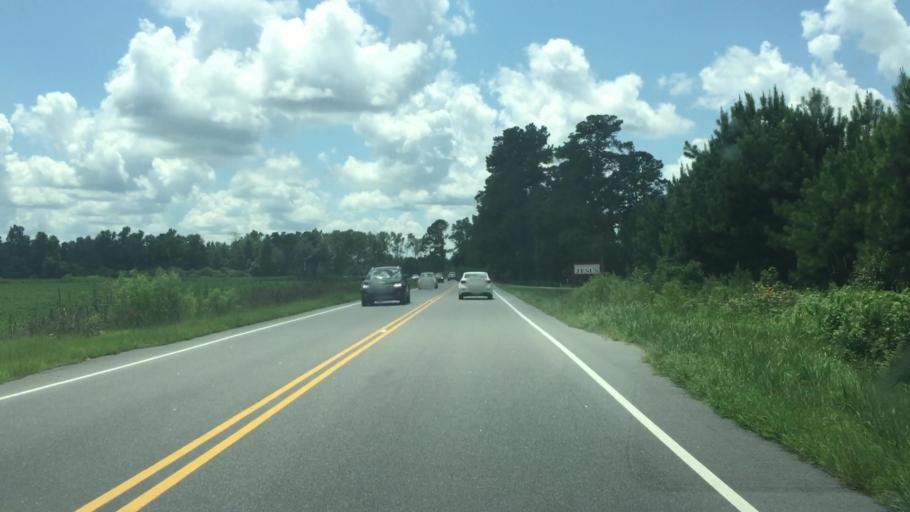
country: US
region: North Carolina
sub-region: Columbus County
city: Tabor City
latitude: 34.2000
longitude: -78.8332
